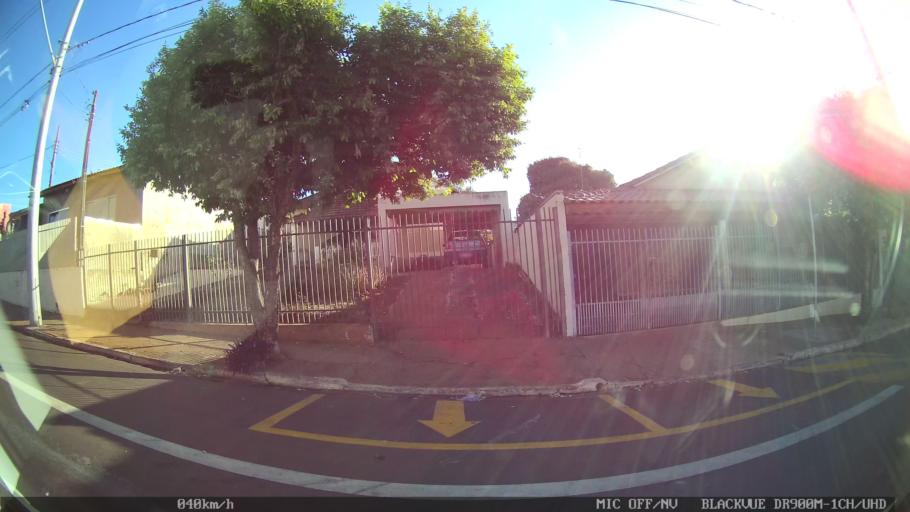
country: BR
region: Sao Paulo
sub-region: Guapiacu
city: Guapiacu
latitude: -20.7921
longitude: -49.2215
